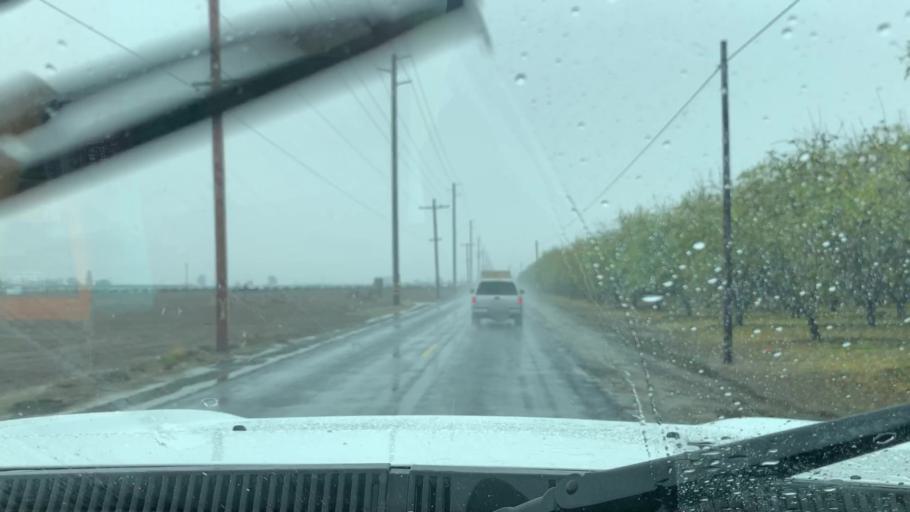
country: US
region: California
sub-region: Tulare County
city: Earlimart
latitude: 35.8339
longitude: -119.2384
